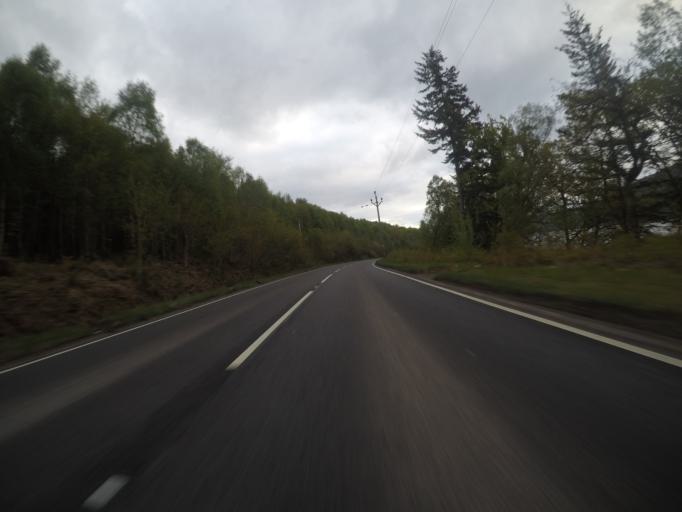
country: GB
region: Scotland
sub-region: Highland
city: Beauly
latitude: 57.1714
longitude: -4.6444
